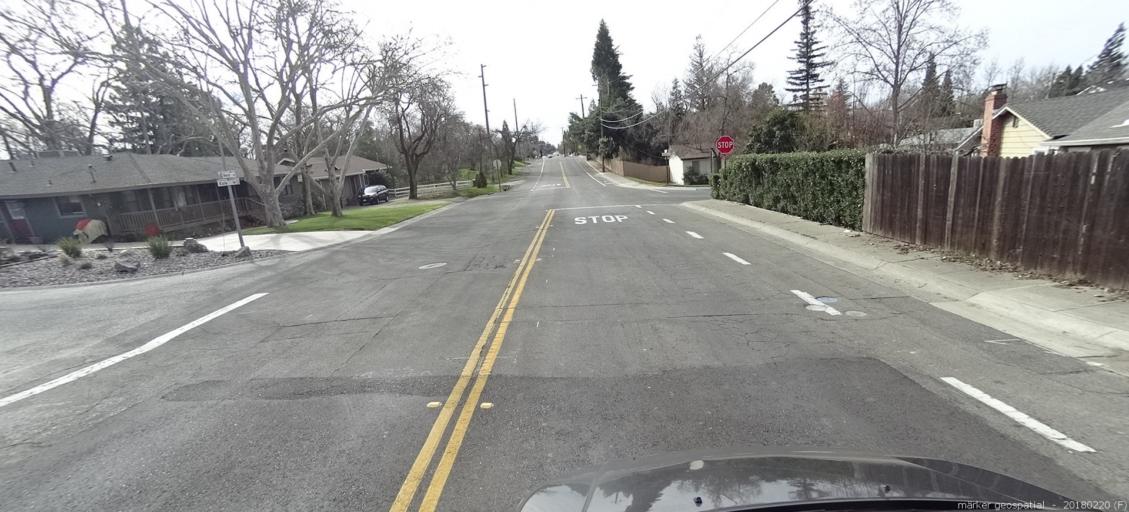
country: US
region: California
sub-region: Sacramento County
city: Orangevale
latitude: 38.6883
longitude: -121.2302
